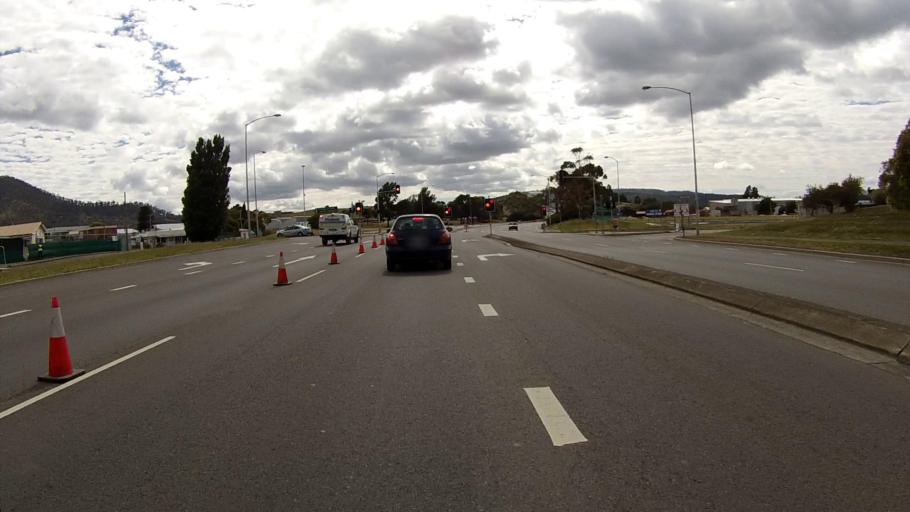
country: AU
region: Tasmania
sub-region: Glenorchy
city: Goodwood
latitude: -42.8235
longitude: 147.2941
